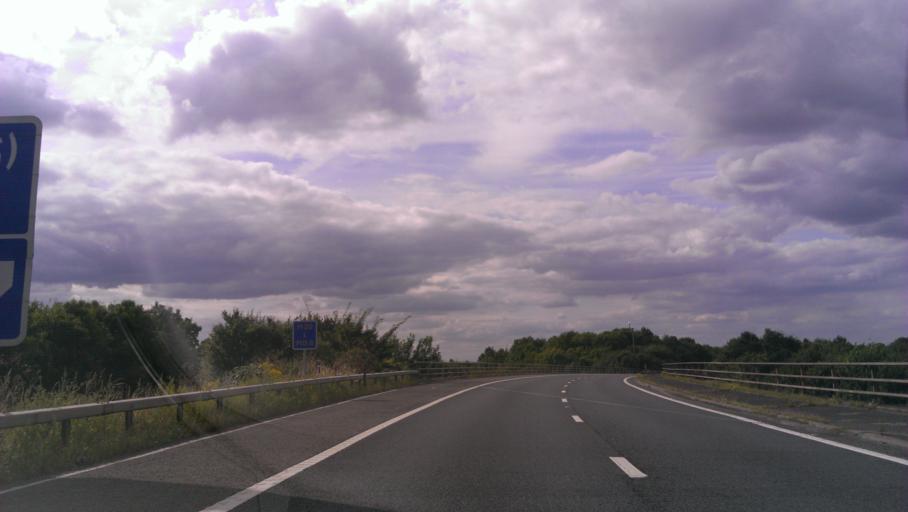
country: GB
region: England
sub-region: Kent
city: Eynsford
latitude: 51.3868
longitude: 0.1992
